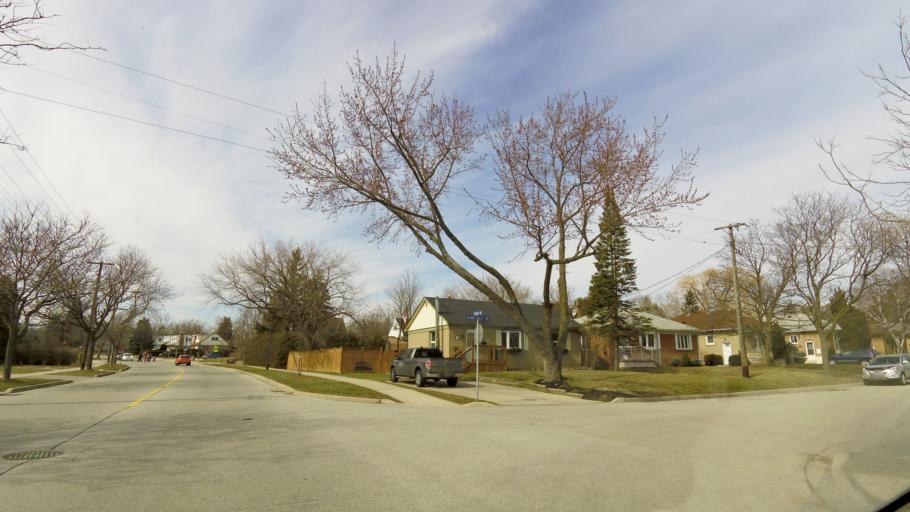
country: CA
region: Ontario
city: Burlington
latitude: 43.3570
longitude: -79.8219
